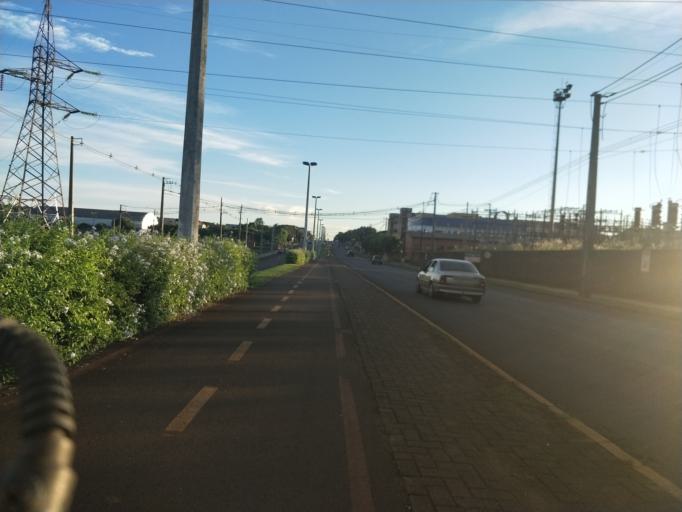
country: BR
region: Parana
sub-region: Marechal Candido Rondon
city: Marechal Candido Rondon
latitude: -24.5551
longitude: -54.0473
